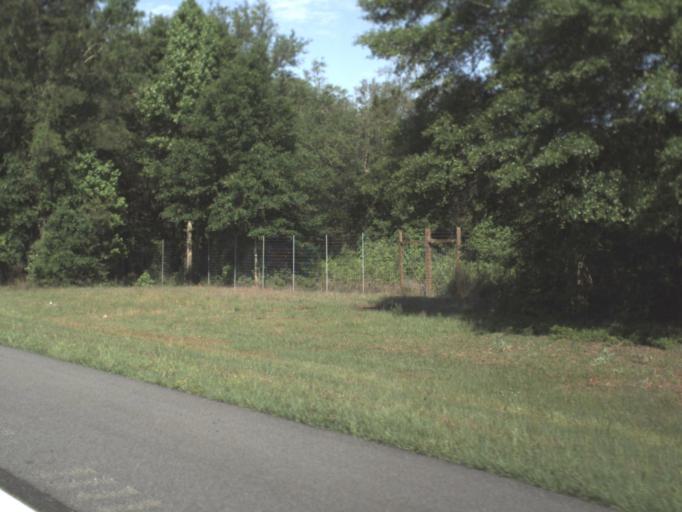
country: US
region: Florida
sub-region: Walton County
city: DeFuniak Springs
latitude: 30.7253
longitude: -85.9084
